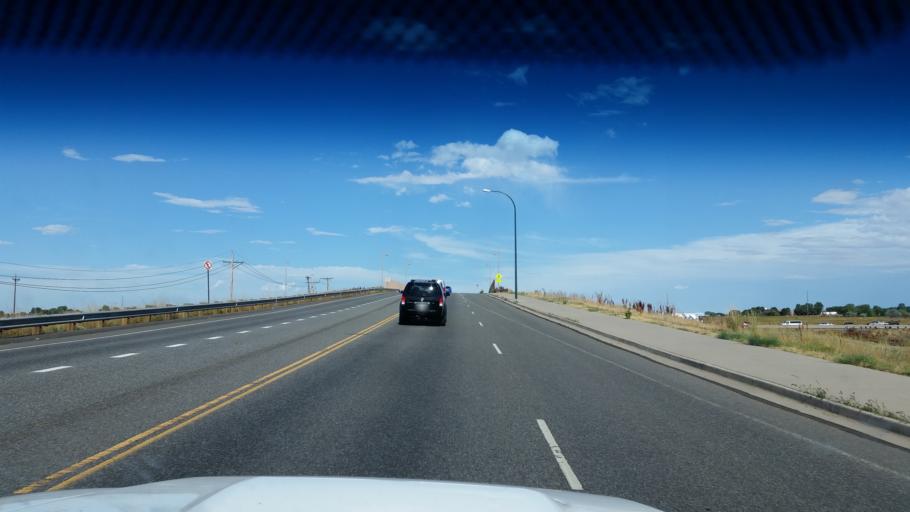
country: US
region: Colorado
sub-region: Adams County
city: Northglenn
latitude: 39.9285
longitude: -104.9902
